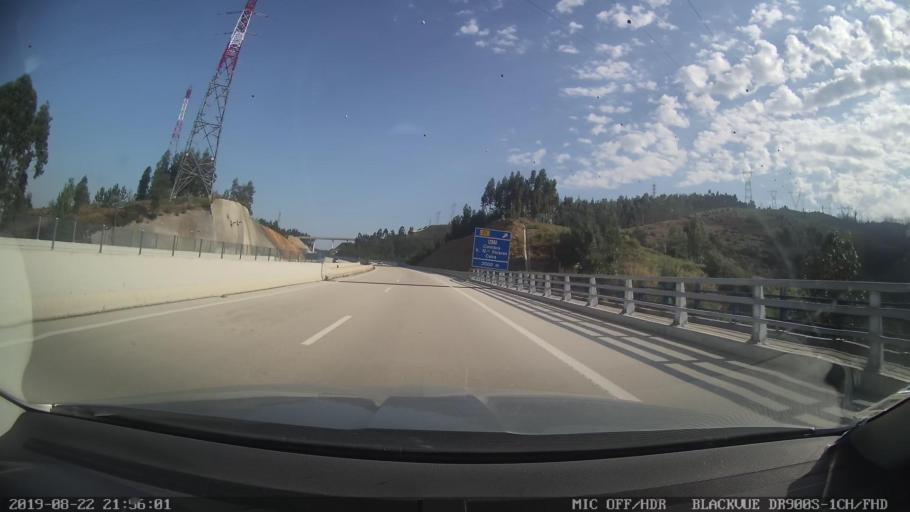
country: PT
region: Coimbra
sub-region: Coimbra
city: Coimbra
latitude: 40.1630
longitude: -8.3778
